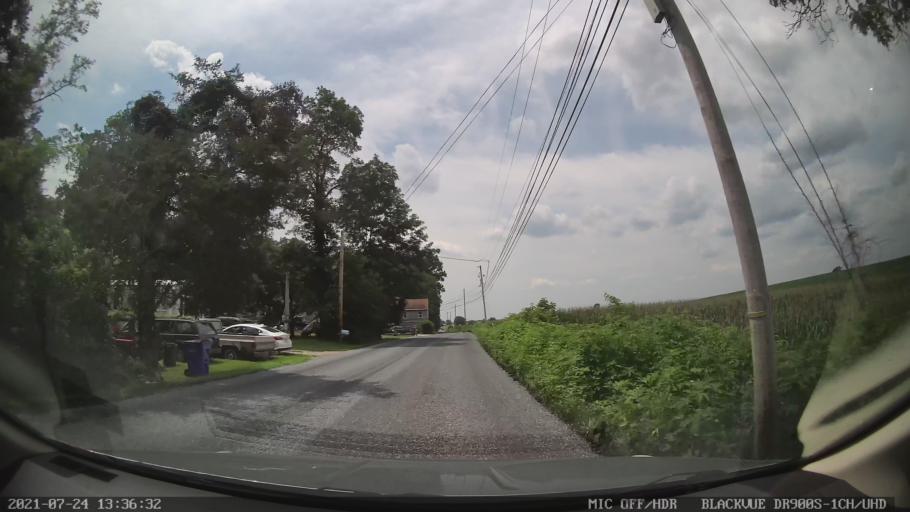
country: US
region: Pennsylvania
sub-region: Berks County
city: Fleetwood
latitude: 40.4653
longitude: -75.7814
